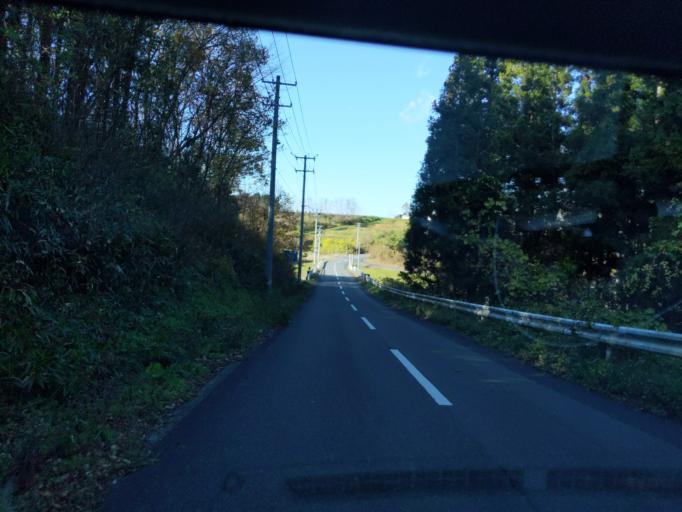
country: JP
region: Iwate
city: Mizusawa
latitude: 39.0708
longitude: 141.1132
